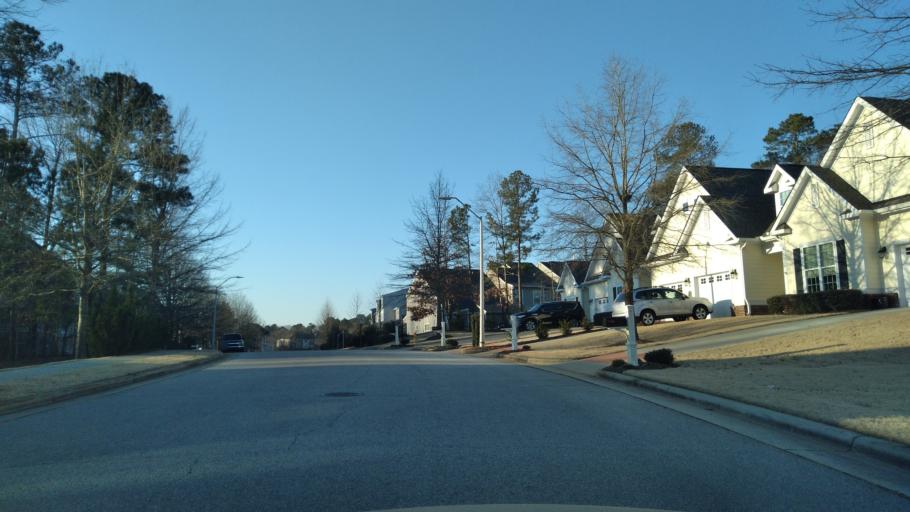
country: US
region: North Carolina
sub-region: Wake County
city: Garner
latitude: 35.6944
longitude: -78.6127
